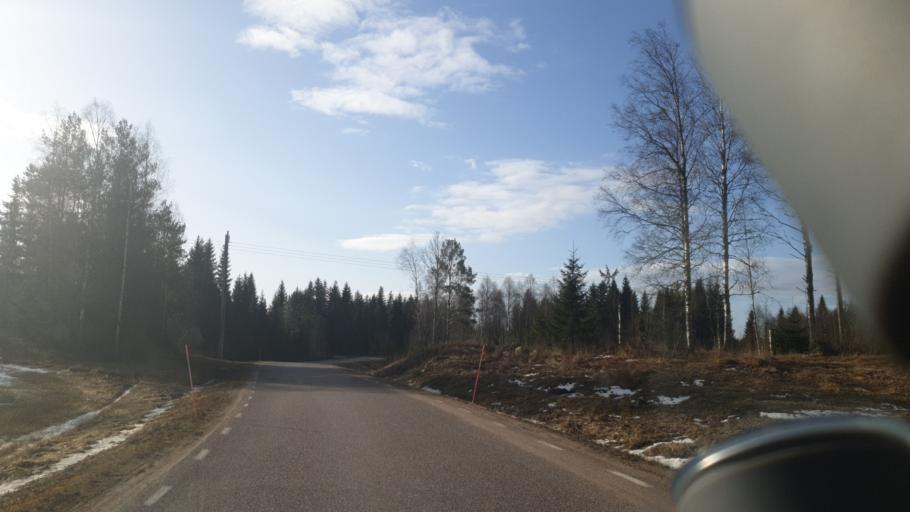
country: SE
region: Vaermland
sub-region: Arvika Kommun
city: Arvika
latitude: 59.7582
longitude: 12.8229
